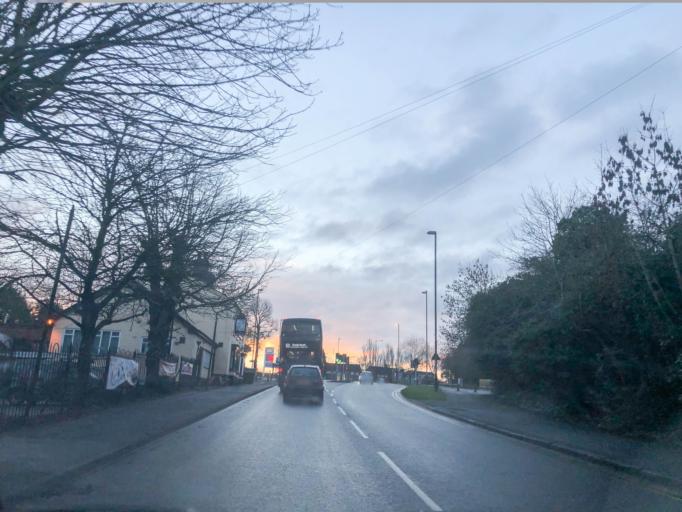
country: GB
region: England
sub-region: Solihull
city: Tidbury Green
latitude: 52.4148
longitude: -1.8866
